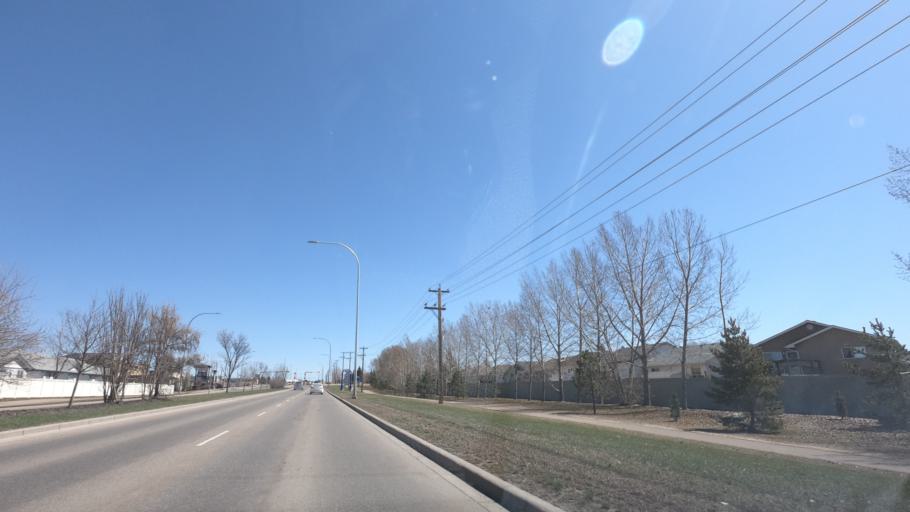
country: CA
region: Alberta
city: Airdrie
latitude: 51.2999
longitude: -114.0171
